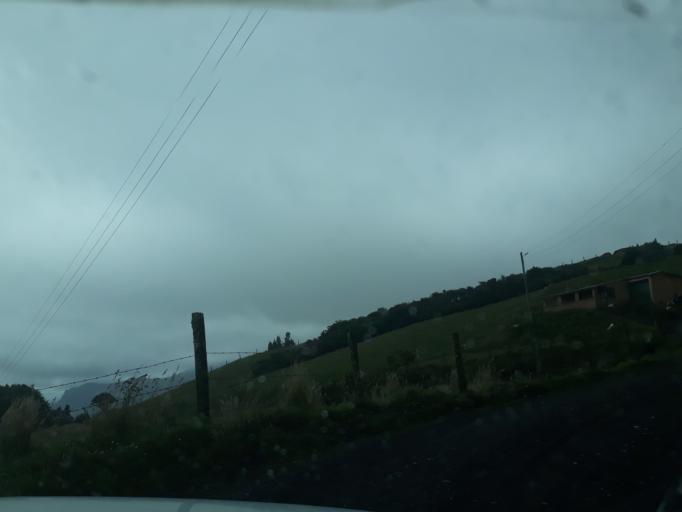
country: CO
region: Cundinamarca
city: La Mesa
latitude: 5.2406
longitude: -74.0283
